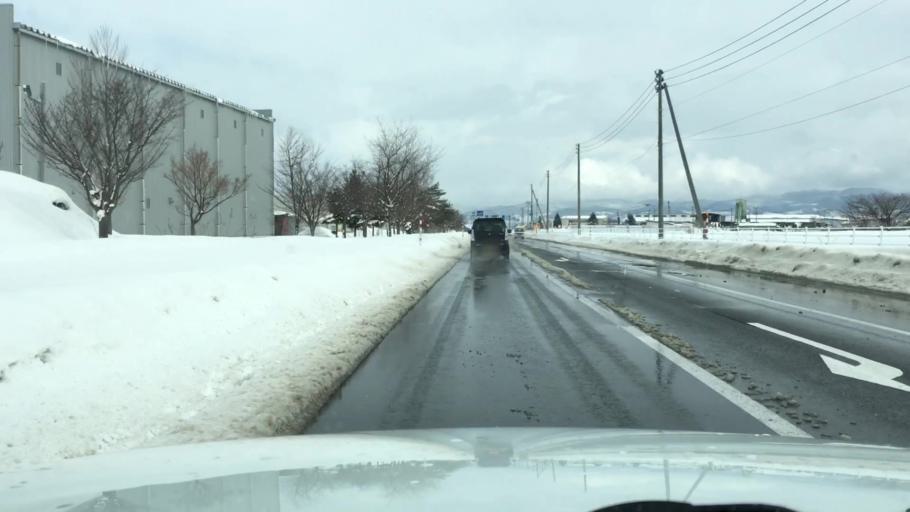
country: JP
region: Aomori
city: Hirosaki
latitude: 40.5852
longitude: 140.5034
